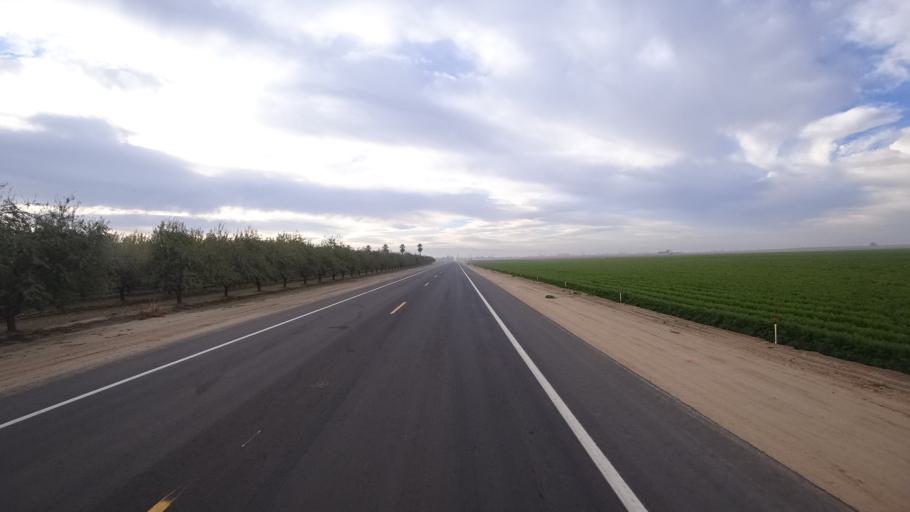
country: US
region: California
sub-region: Kern County
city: Rosedale
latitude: 35.4076
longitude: -119.1988
